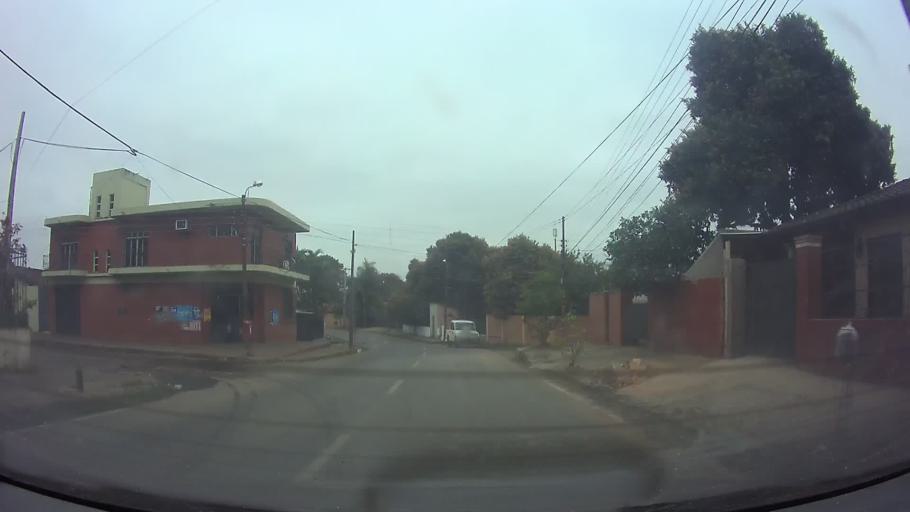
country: PY
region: Central
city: Lambare
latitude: -25.3221
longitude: -57.5673
